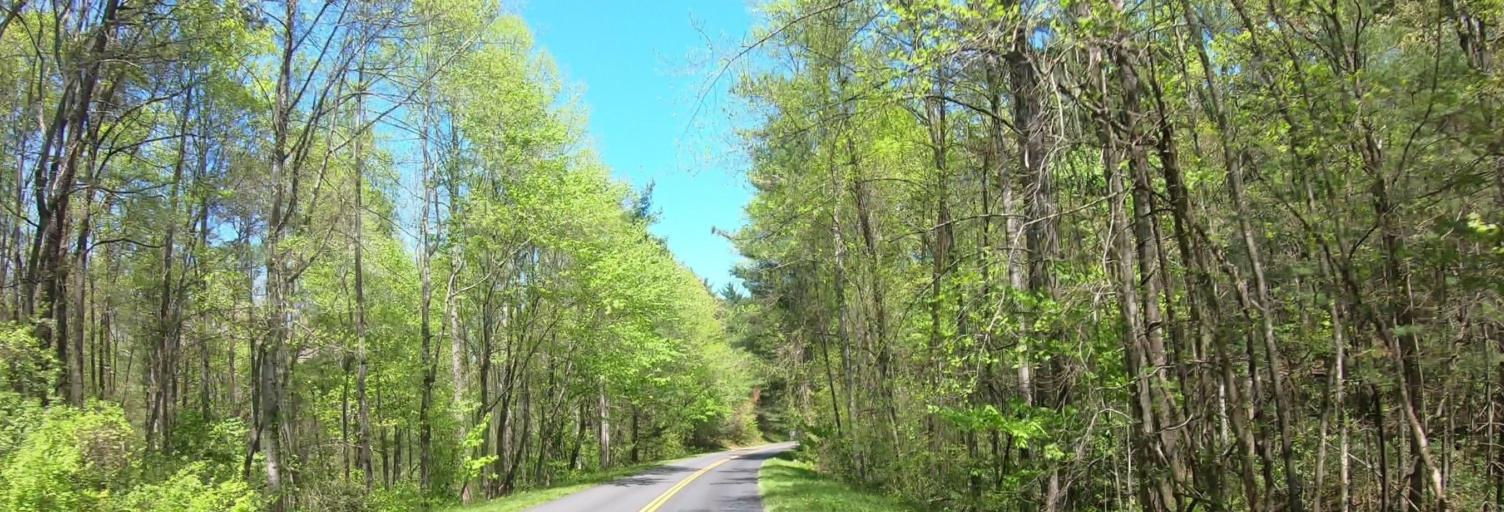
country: US
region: North Carolina
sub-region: Buncombe County
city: Biltmore Forest
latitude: 35.5604
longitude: -82.4952
